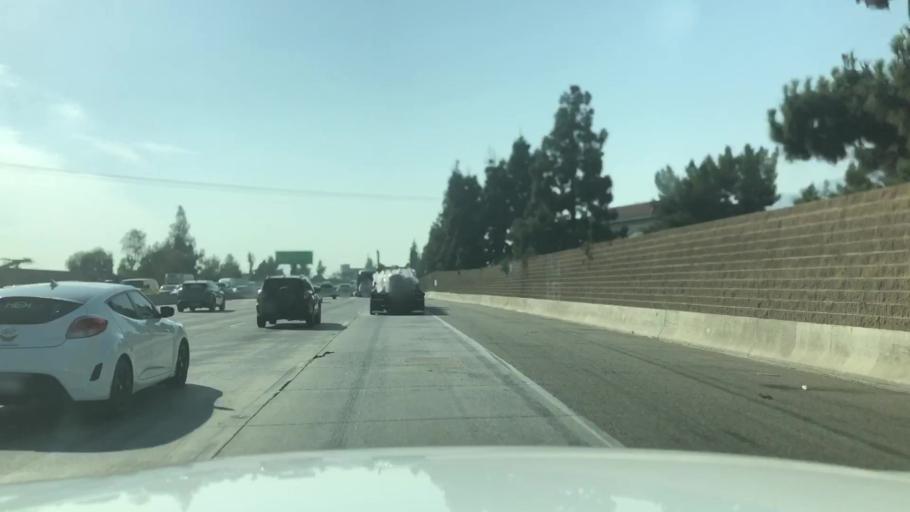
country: US
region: California
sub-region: Los Angeles County
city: Monrovia
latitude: 34.1361
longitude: -118.0084
